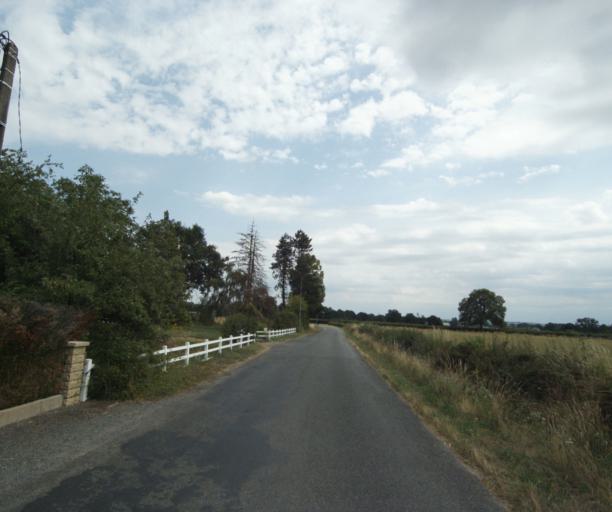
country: FR
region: Bourgogne
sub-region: Departement de Saone-et-Loire
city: Gueugnon
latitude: 46.6093
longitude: 4.0426
